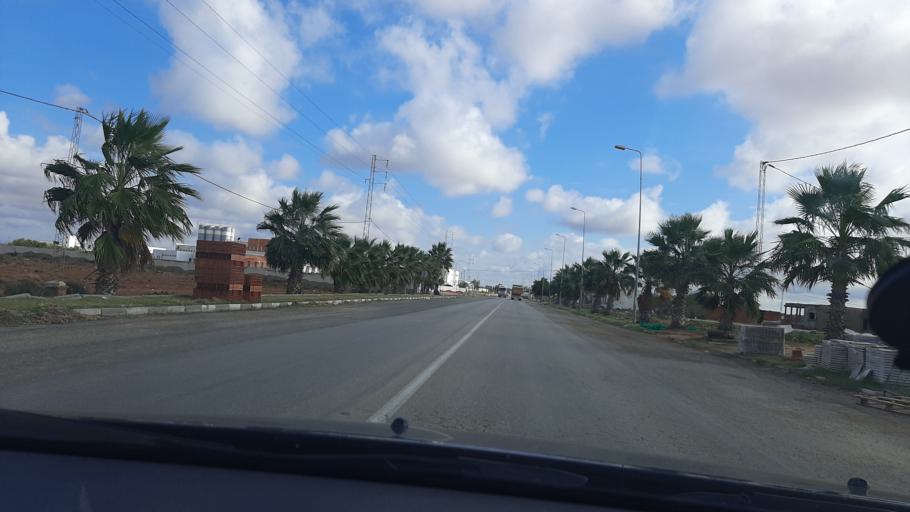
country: TN
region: Al Mahdiyah
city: Shurban
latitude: 34.9640
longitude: 10.3795
